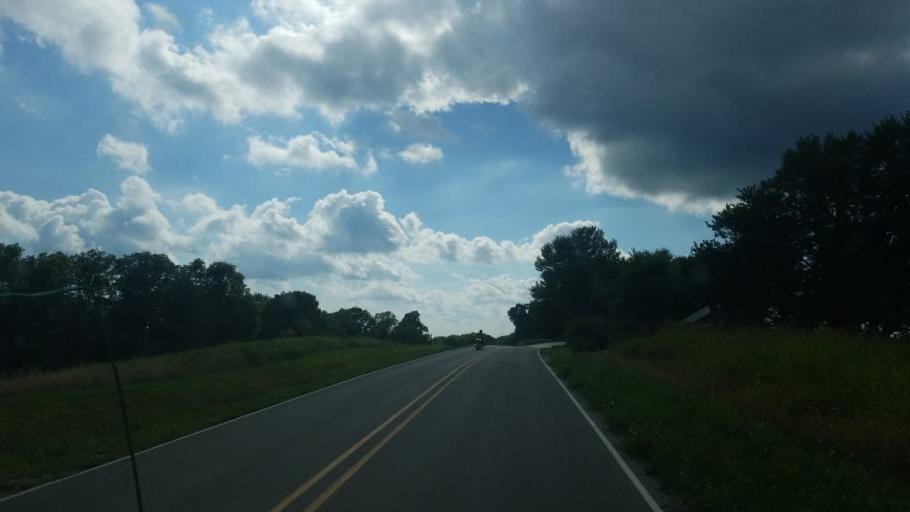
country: US
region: Illinois
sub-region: Union County
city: Cobden
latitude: 37.5475
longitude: -89.2915
